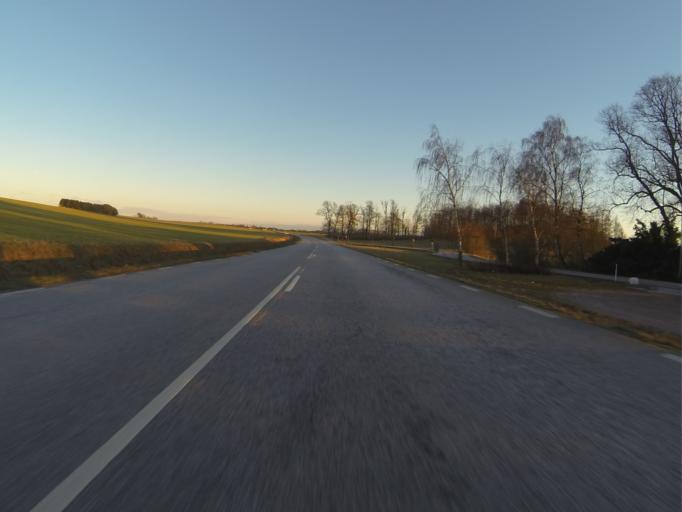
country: SE
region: Skane
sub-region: Eslovs Kommun
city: Eslov
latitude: 55.7613
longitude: 13.3280
